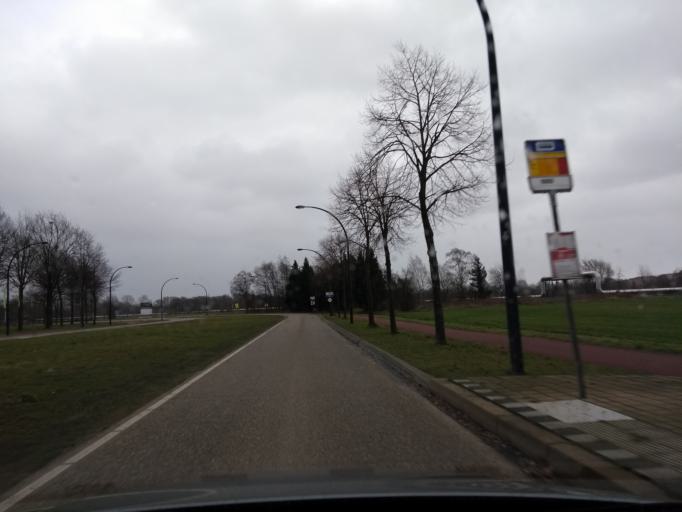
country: NL
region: Overijssel
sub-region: Gemeente Hengelo
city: Hengelo
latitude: 52.2400
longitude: 6.7863
